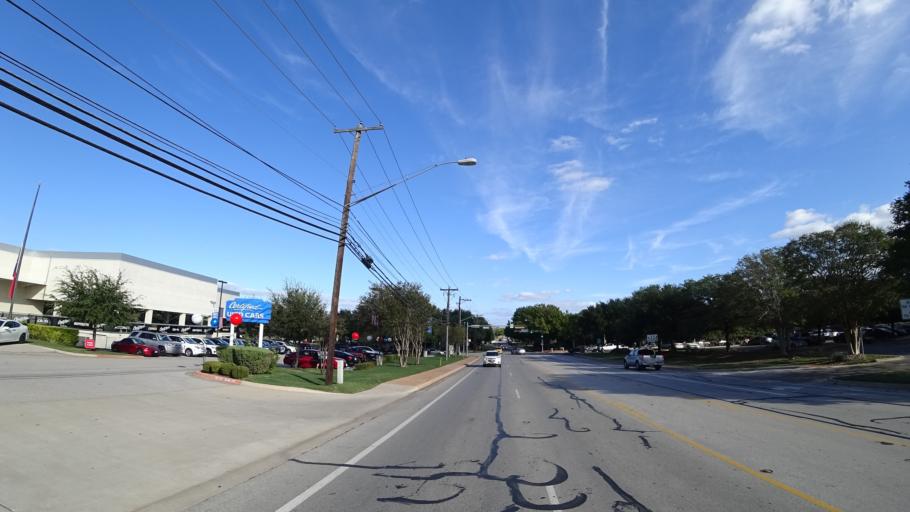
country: US
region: Texas
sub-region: Williamson County
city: Jollyville
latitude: 30.3667
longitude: -97.7392
